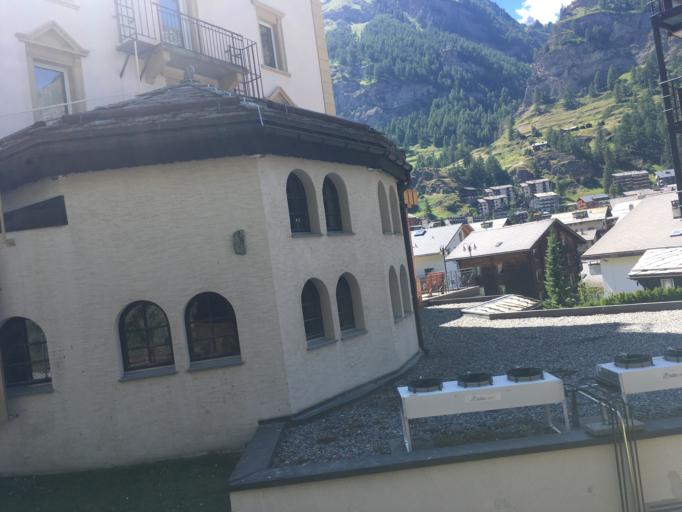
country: CH
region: Valais
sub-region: Visp District
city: Zermatt
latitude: 46.0207
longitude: 7.7510
